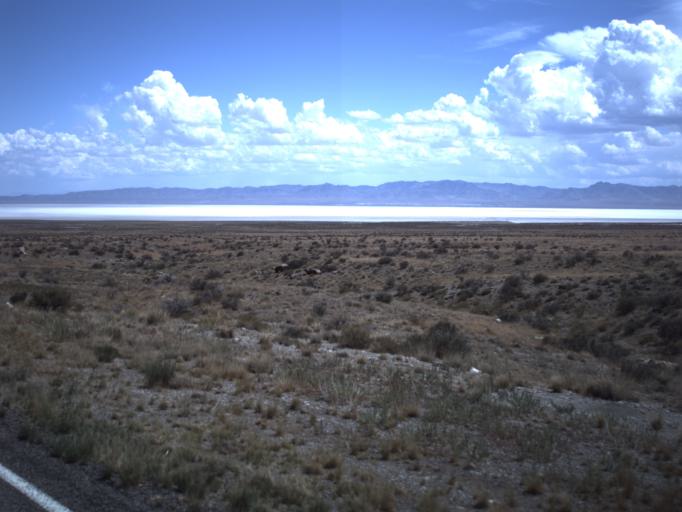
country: US
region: Utah
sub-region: Beaver County
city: Milford
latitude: 39.0519
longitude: -113.2686
